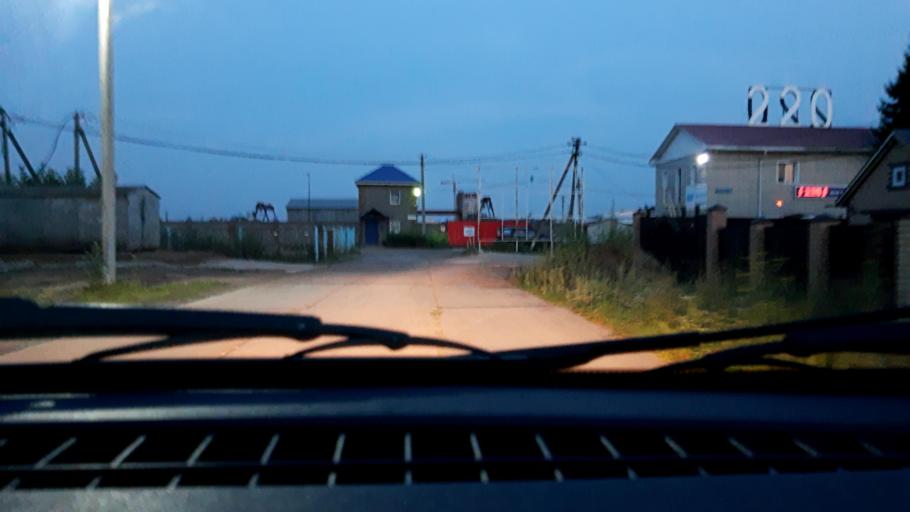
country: RU
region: Bashkortostan
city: Mikhaylovka
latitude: 54.8036
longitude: 55.8727
